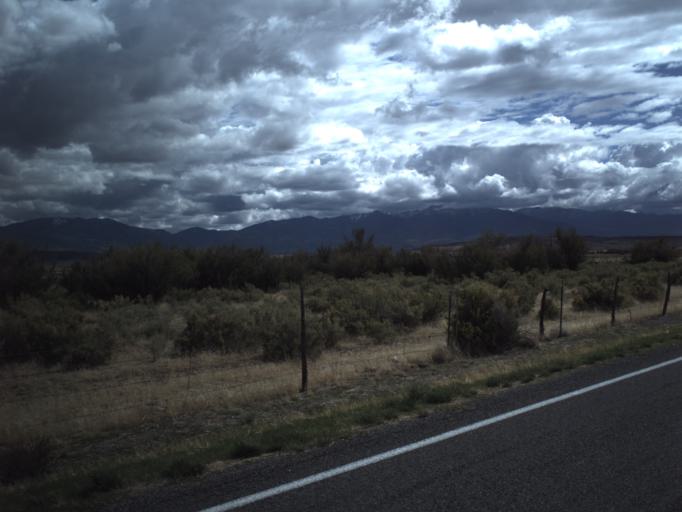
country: US
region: Utah
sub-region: Millard County
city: Fillmore
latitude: 39.0682
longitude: -112.4098
